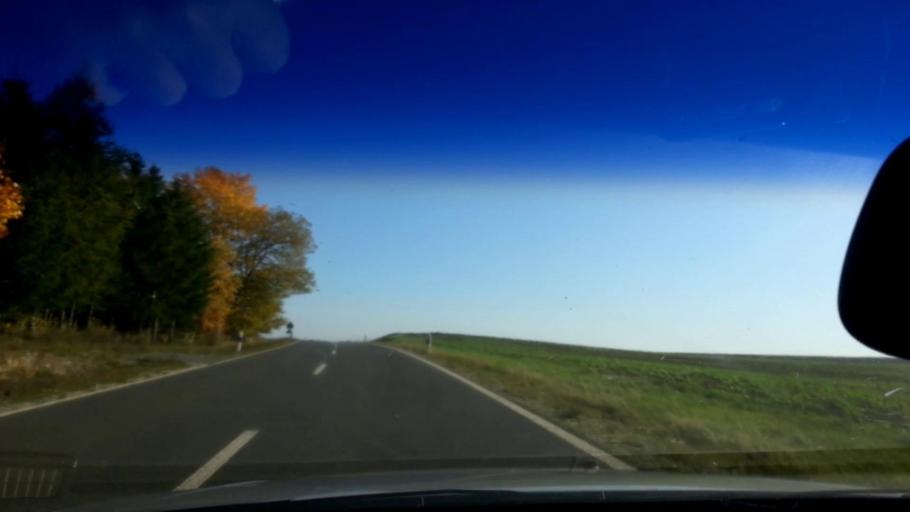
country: DE
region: Bavaria
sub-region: Upper Franconia
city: Wonsees
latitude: 49.9793
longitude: 11.2815
